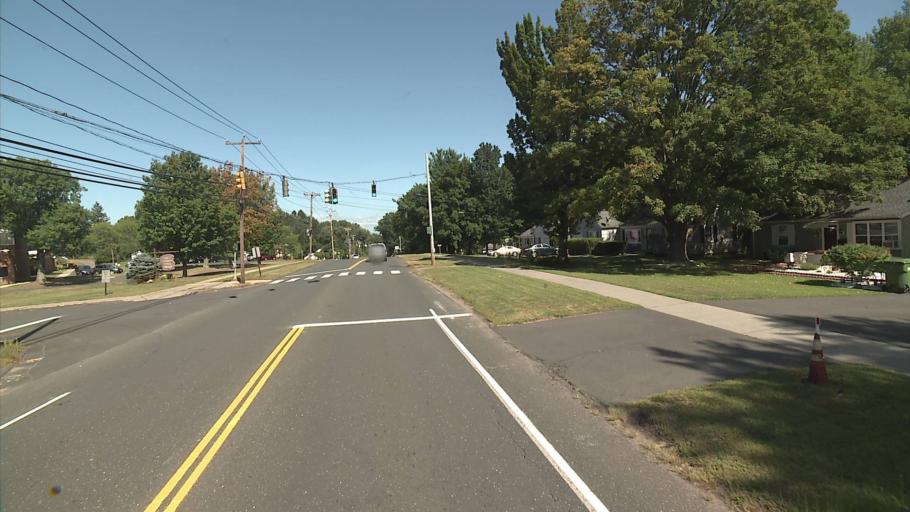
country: US
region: Connecticut
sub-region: Hartford County
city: Blue Hills
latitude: 41.8364
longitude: -72.6754
